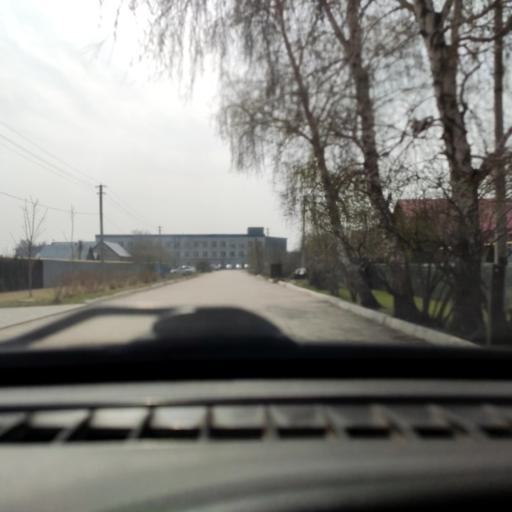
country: RU
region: Samara
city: Tol'yatti
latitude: 53.5752
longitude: 49.3049
